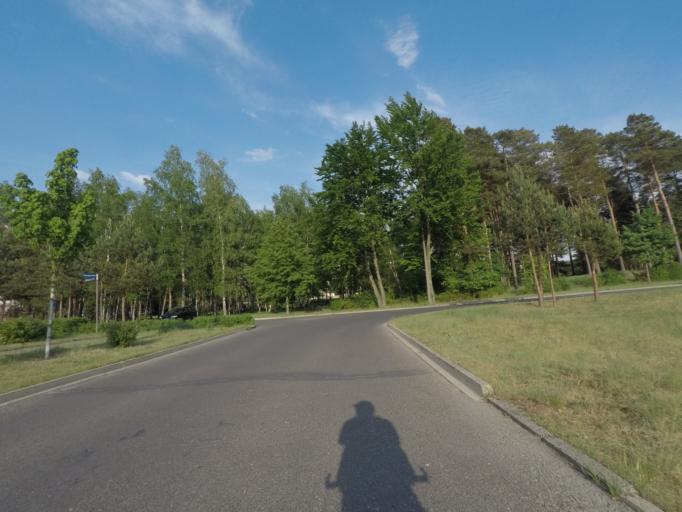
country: DE
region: Brandenburg
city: Eberswalde
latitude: 52.8296
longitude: 13.7572
